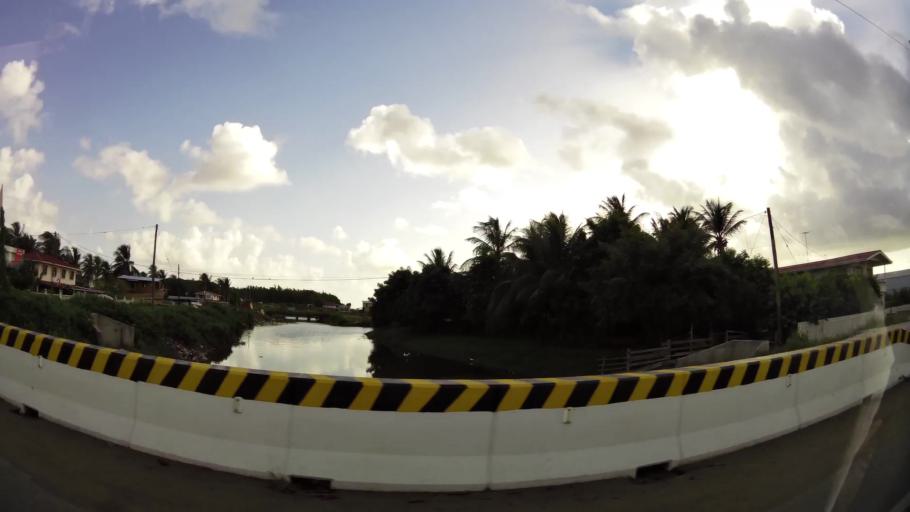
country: GY
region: Demerara-Mahaica
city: Georgetown
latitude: 6.8040
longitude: -58.0477
